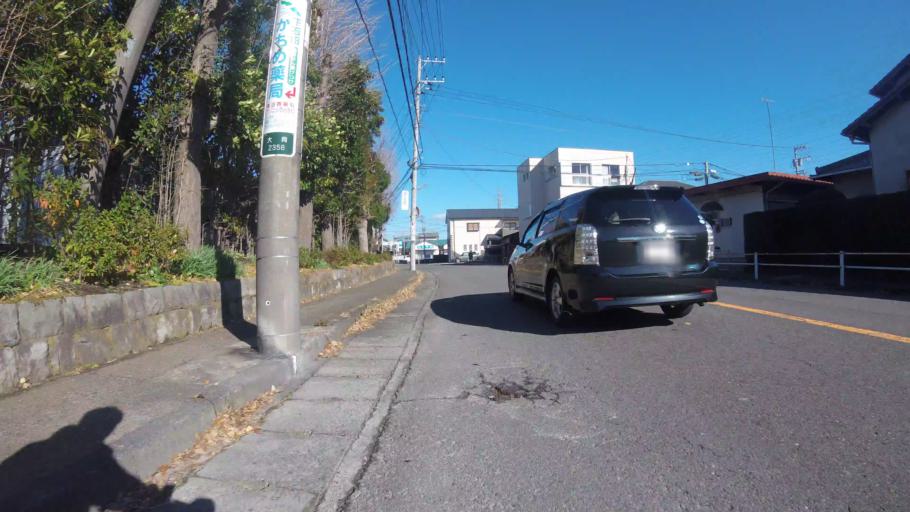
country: JP
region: Shizuoka
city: Numazu
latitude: 35.1125
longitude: 138.8805
